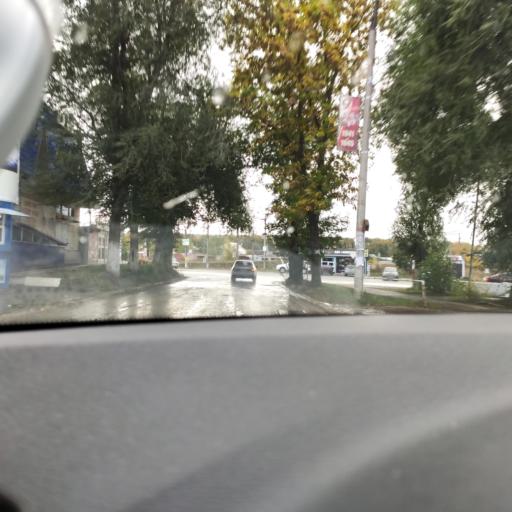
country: RU
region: Samara
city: Novosemeykino
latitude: 53.3701
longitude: 50.3541
